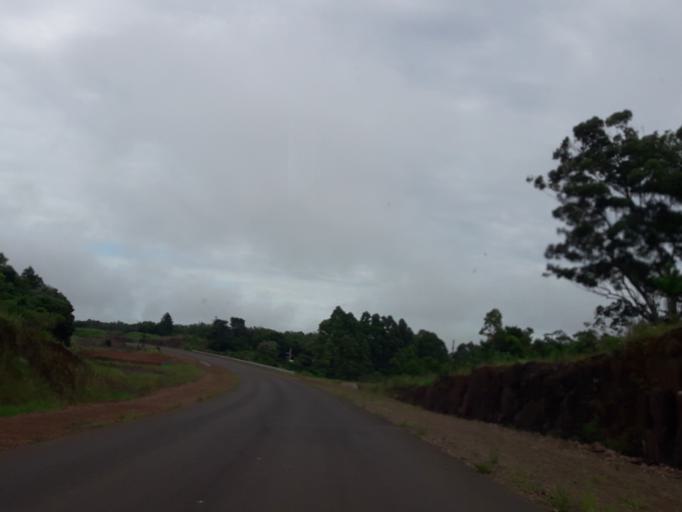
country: AR
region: Misiones
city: Bernardo de Irigoyen
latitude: -26.4271
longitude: -53.8475
